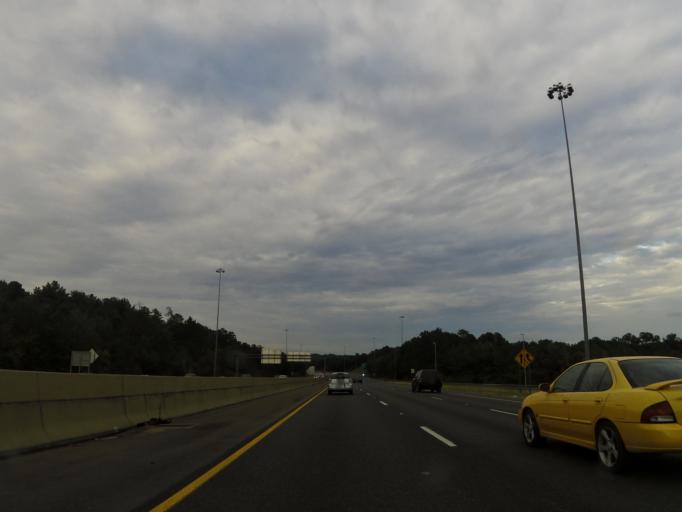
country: US
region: Alabama
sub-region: Shelby County
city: Indian Springs Village
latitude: 33.3577
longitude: -86.7783
